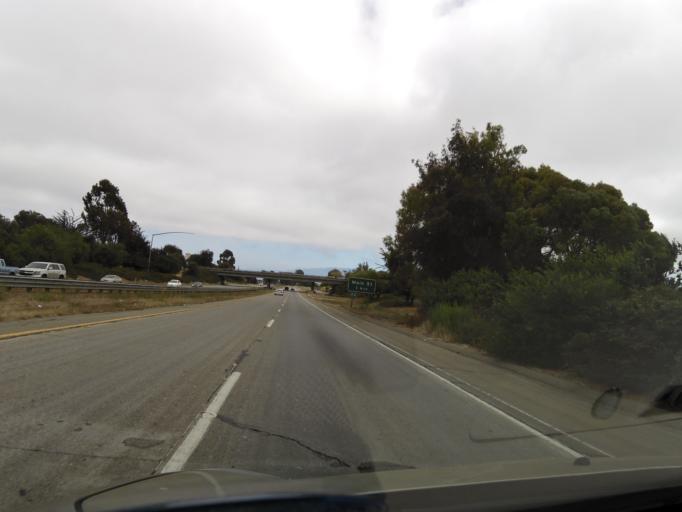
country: US
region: California
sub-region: Monterey County
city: Boronda
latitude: 36.6999
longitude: -121.6656
